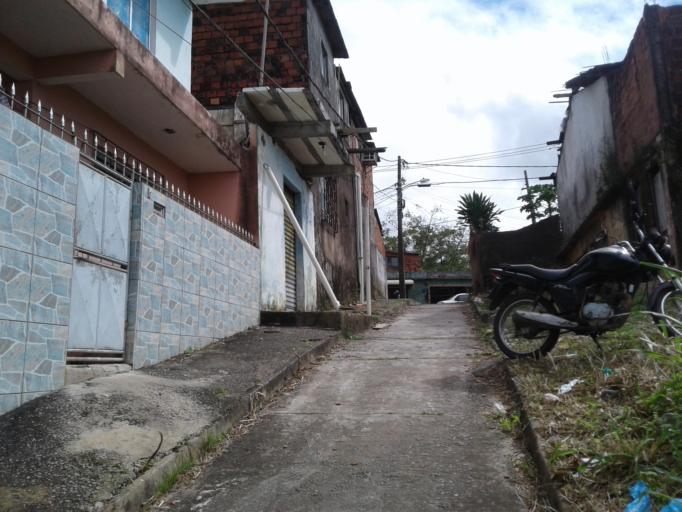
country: BR
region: Bahia
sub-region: Salvador
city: Salvador
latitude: -12.9085
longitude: -38.4745
